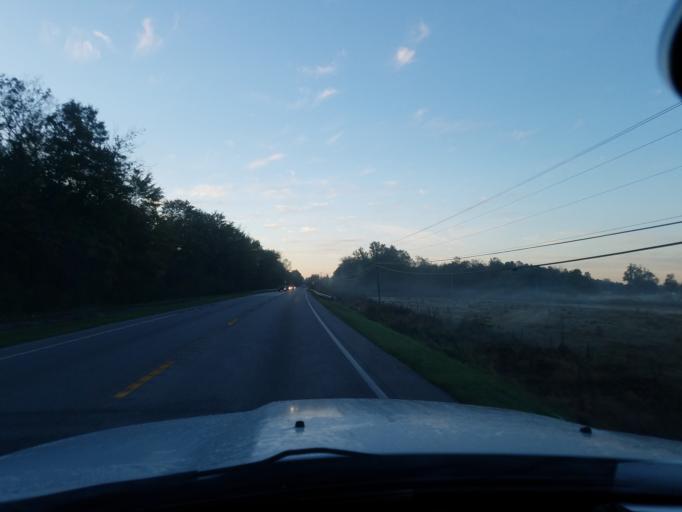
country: US
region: Kentucky
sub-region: Laurel County
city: London
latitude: 37.0823
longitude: -84.0601
